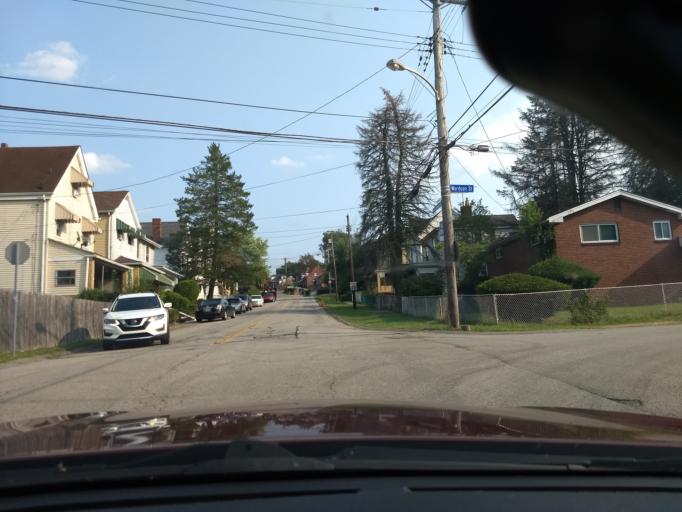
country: US
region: Pennsylvania
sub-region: Allegheny County
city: Aspinwall
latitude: 40.4726
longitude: -79.8967
